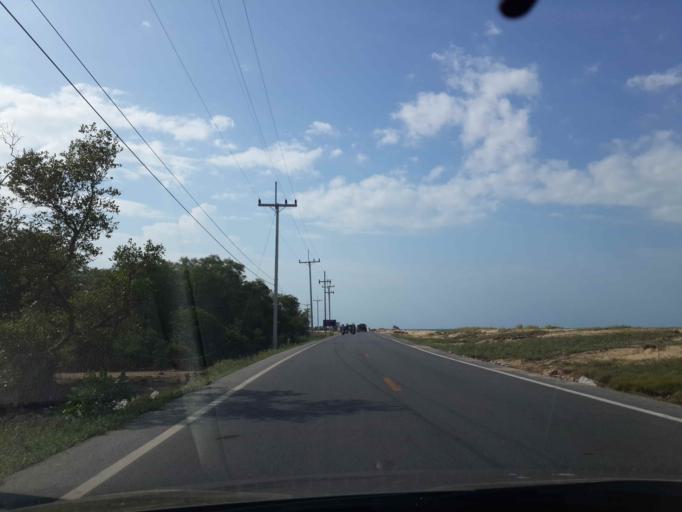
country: TH
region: Pattani
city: Yaring
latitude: 6.9223
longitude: 101.3303
